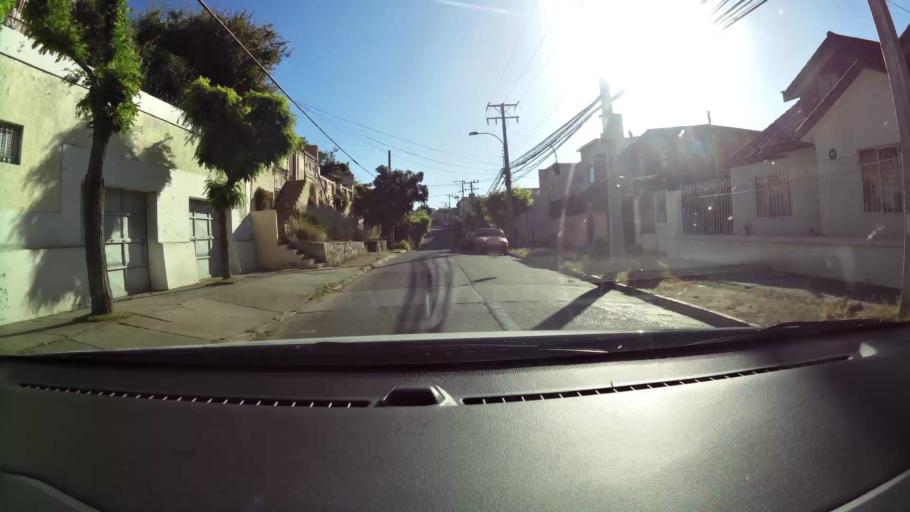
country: CL
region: Valparaiso
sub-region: Provincia de Valparaiso
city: Vina del Mar
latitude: -33.0290
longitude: -71.5725
